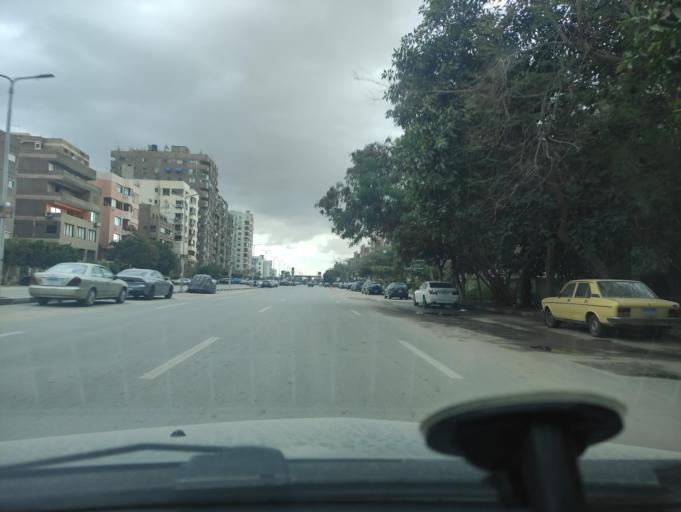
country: EG
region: Muhafazat al Qahirah
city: Cairo
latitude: 30.0491
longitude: 31.3510
